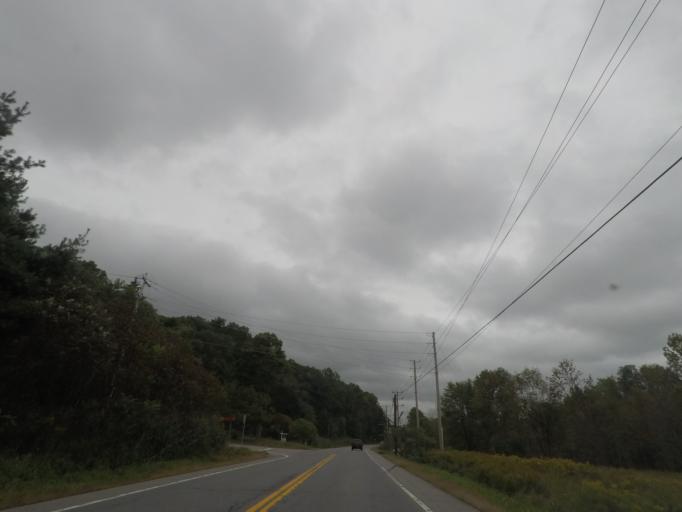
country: US
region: New York
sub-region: Saratoga County
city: Country Knolls
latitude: 42.9246
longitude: -73.7551
